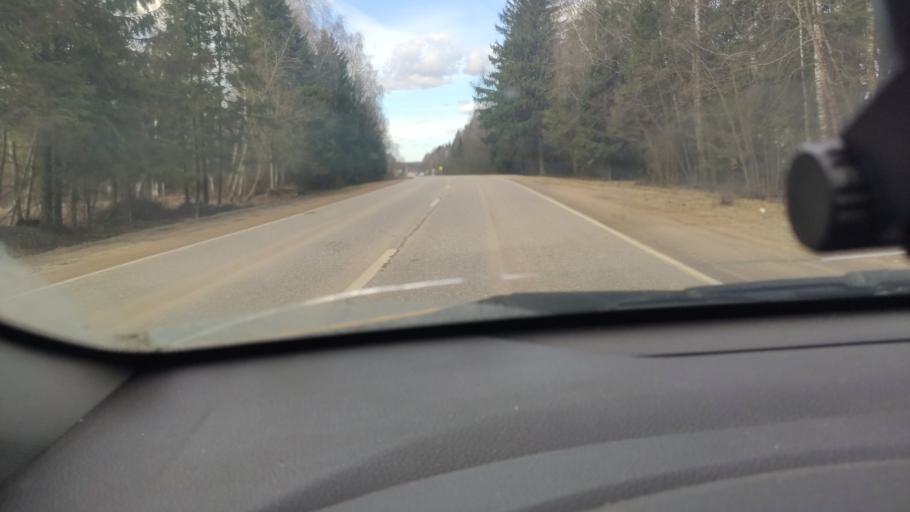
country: RU
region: Moskovskaya
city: Ruza
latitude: 55.7271
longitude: 36.1545
